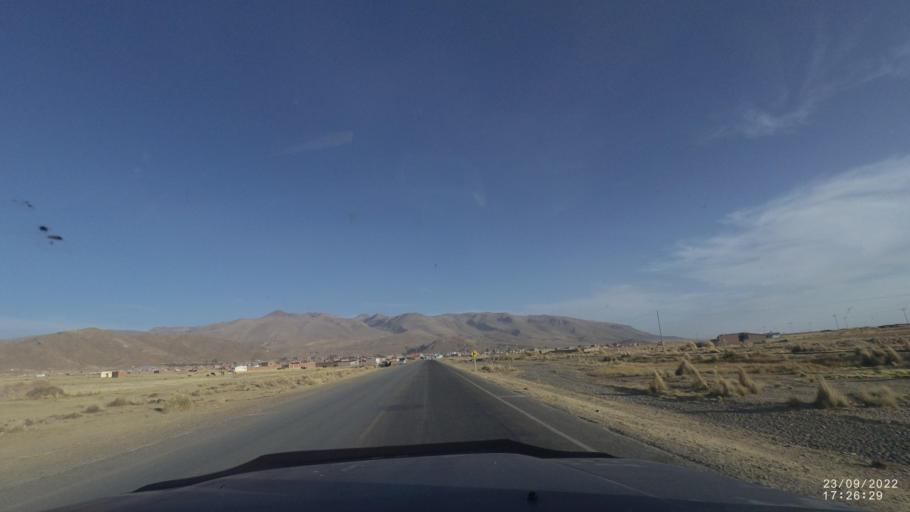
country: BO
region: Oruro
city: Challapata
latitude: -18.8855
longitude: -66.7852
